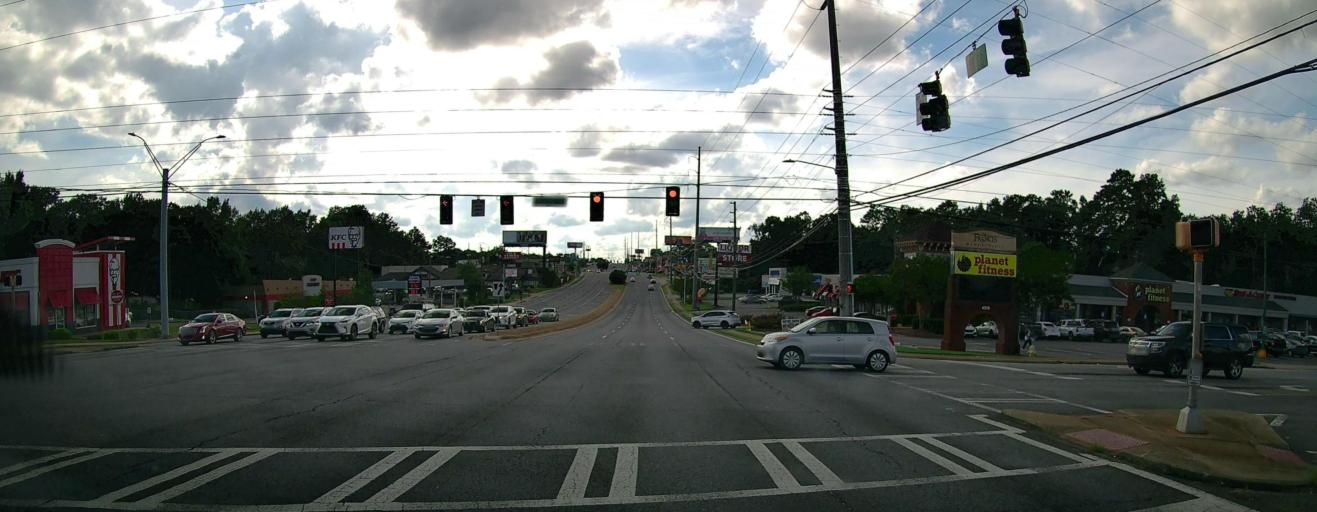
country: US
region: Georgia
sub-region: Muscogee County
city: Columbus
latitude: 32.5071
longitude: -84.9621
